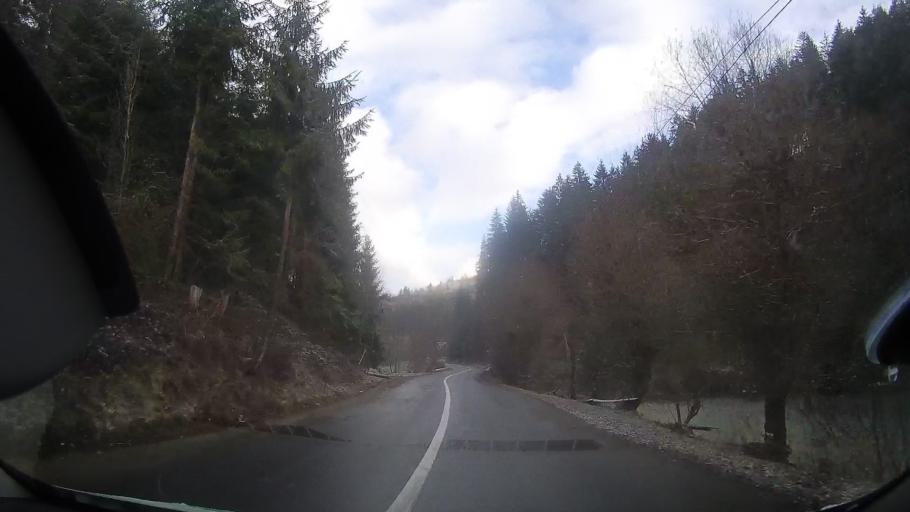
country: RO
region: Alba
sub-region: Comuna Albac
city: Albac
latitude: 46.4551
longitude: 22.9742
